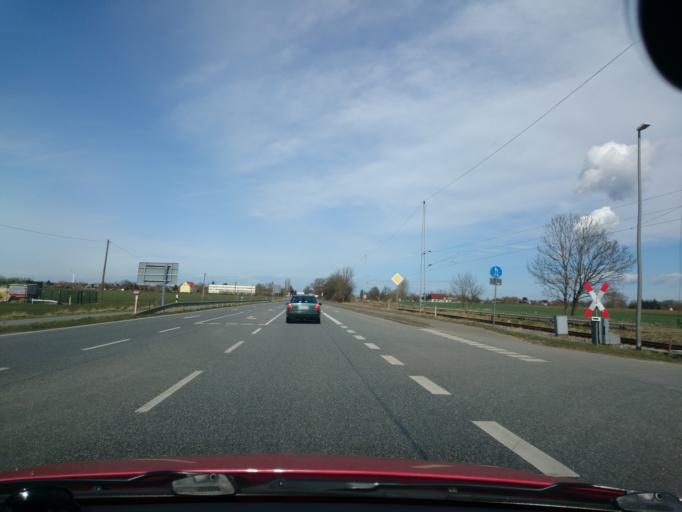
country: DE
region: Mecklenburg-Vorpommern
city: Monchhagen
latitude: 54.1410
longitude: 12.2233
